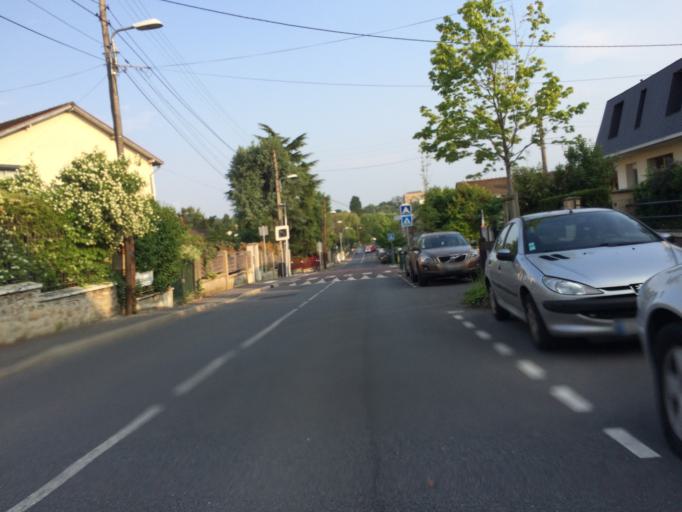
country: FR
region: Ile-de-France
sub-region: Departement de l'Essonne
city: Verrieres-le-Buisson
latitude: 48.7394
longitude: 2.2667
